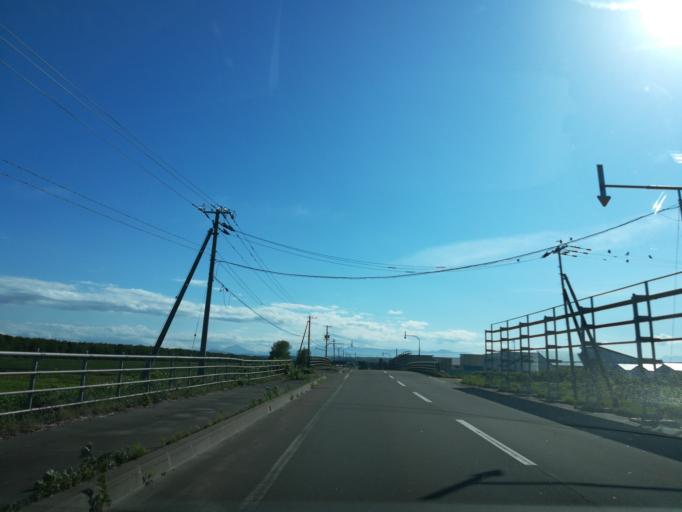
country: JP
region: Hokkaido
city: Kitahiroshima
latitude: 43.0466
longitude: 141.5961
